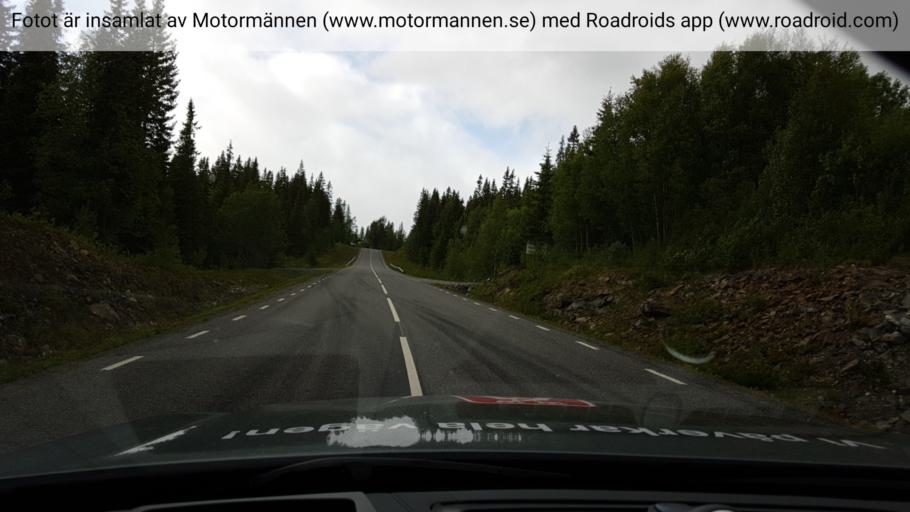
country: SE
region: Jaemtland
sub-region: Are Kommun
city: Are
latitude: 63.6562
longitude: 13.0655
